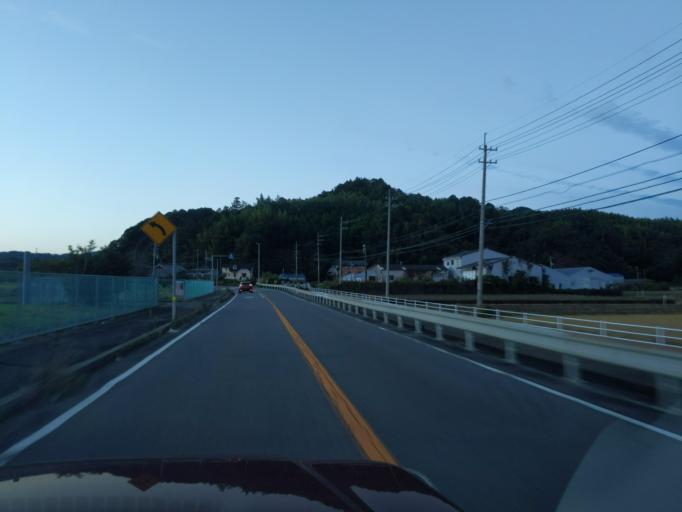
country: JP
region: Tokushima
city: Anan
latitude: 33.8589
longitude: 134.6268
